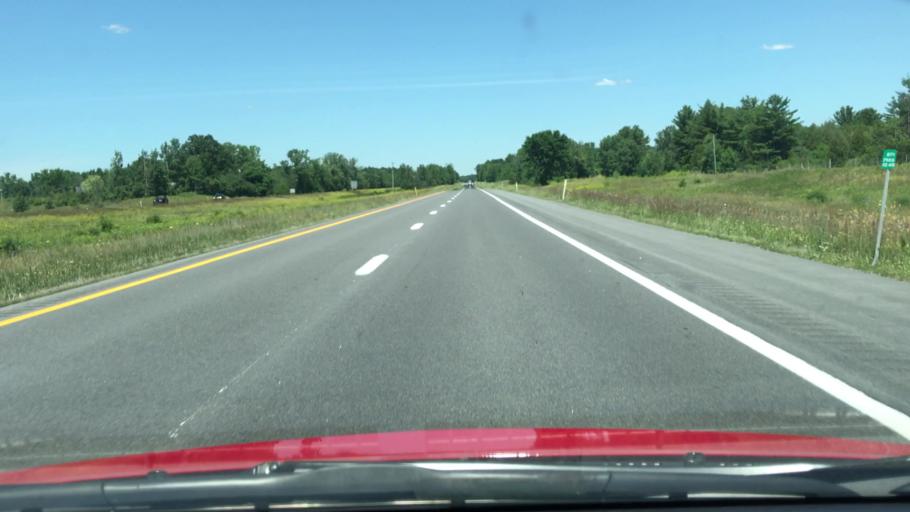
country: US
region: New York
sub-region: Clinton County
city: Cumberland Head
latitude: 44.8202
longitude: -73.4458
